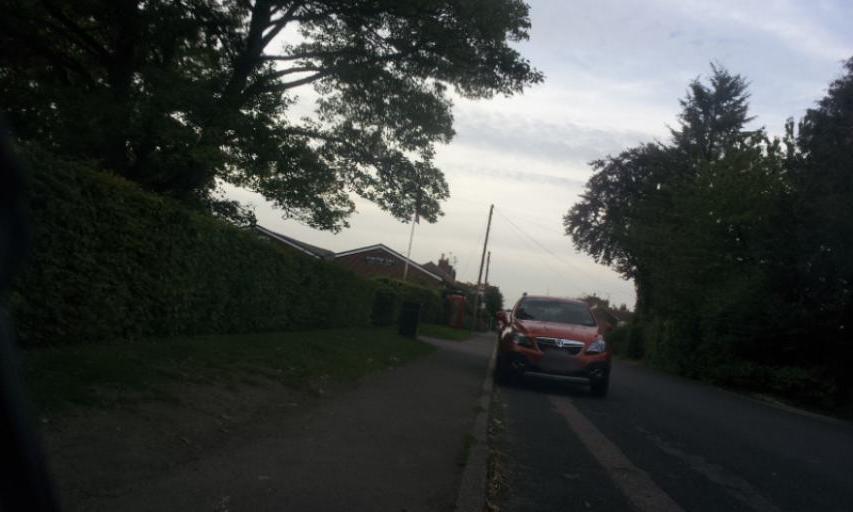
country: GB
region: England
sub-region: Kent
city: Maidstone
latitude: 51.2298
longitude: 0.5324
